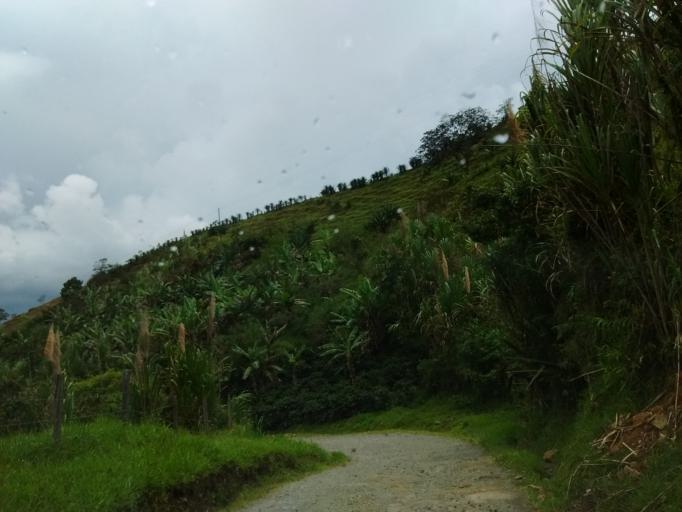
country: CO
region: Cauca
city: Cajibio
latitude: 2.5616
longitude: -76.6331
